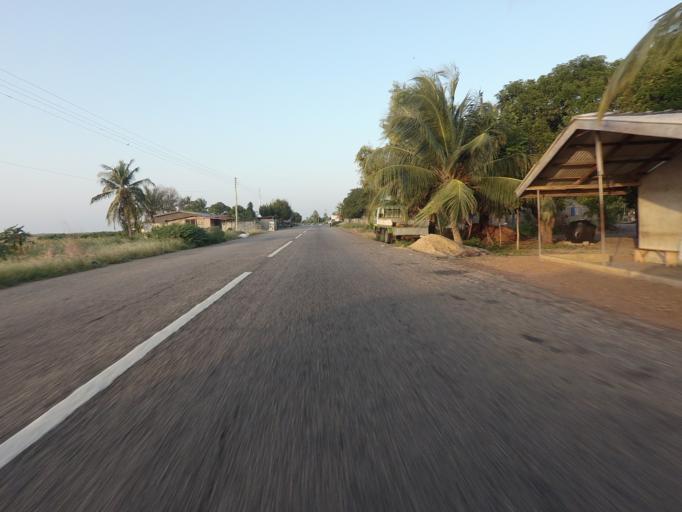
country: GH
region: Volta
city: Anloga
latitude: 5.7843
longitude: 0.8497
